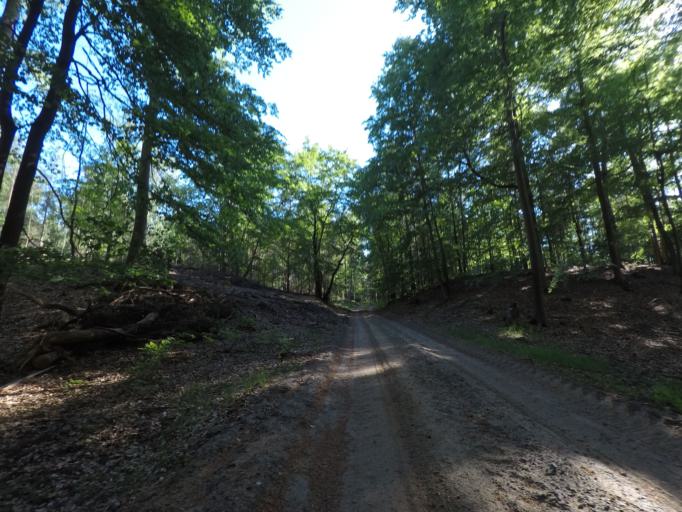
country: DE
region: Brandenburg
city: Marienwerder
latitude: 52.8343
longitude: 13.6333
